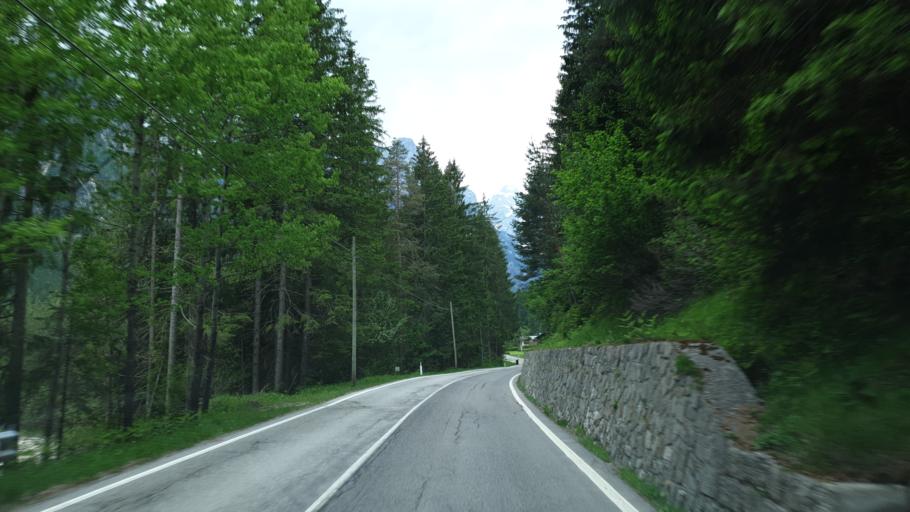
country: IT
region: Veneto
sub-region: Provincia di Belluno
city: Auronzo
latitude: 46.5487
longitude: 12.3281
